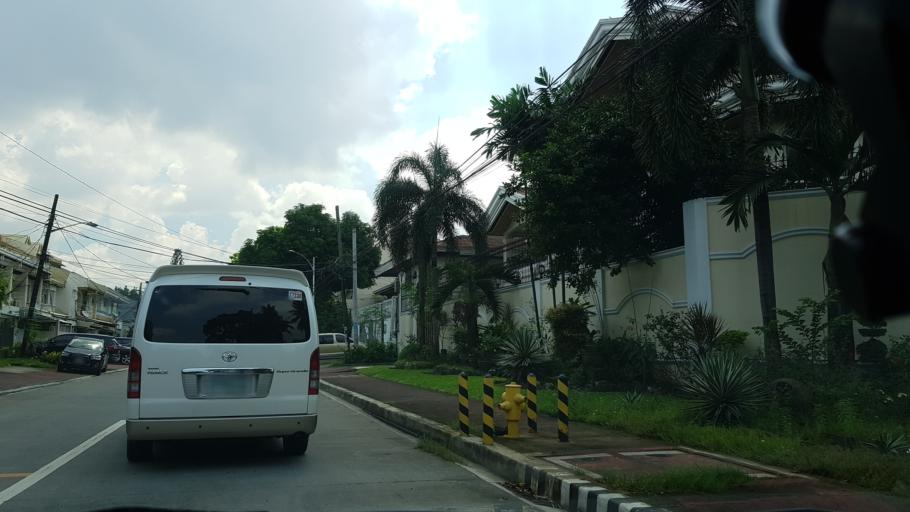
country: PH
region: Calabarzon
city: Del Monte
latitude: 14.6320
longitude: 121.0281
